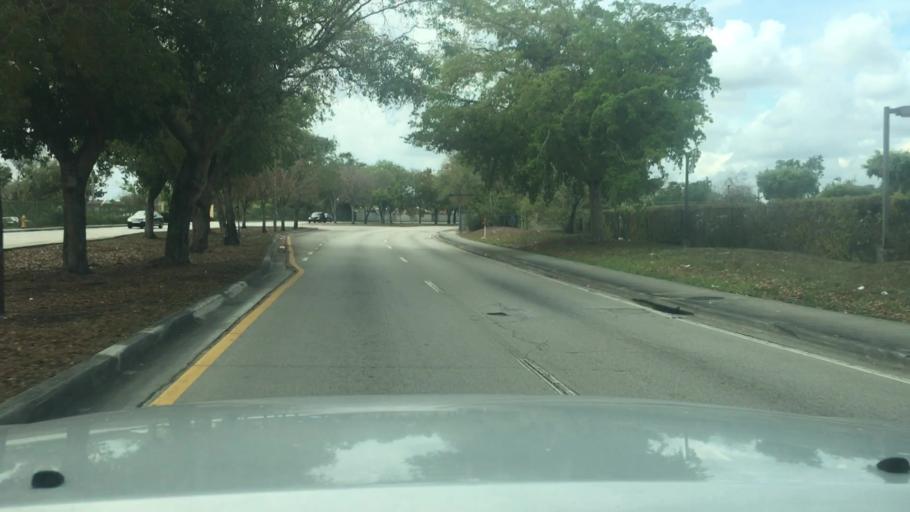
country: US
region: Florida
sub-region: Miami-Dade County
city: Tamiami
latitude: 25.7561
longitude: -80.3915
